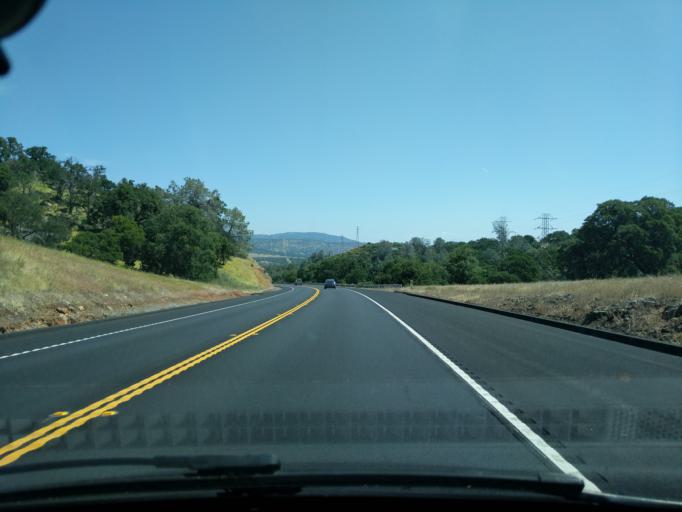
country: US
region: California
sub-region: Calaveras County
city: Copperopolis
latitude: 37.9446
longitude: -120.7007
